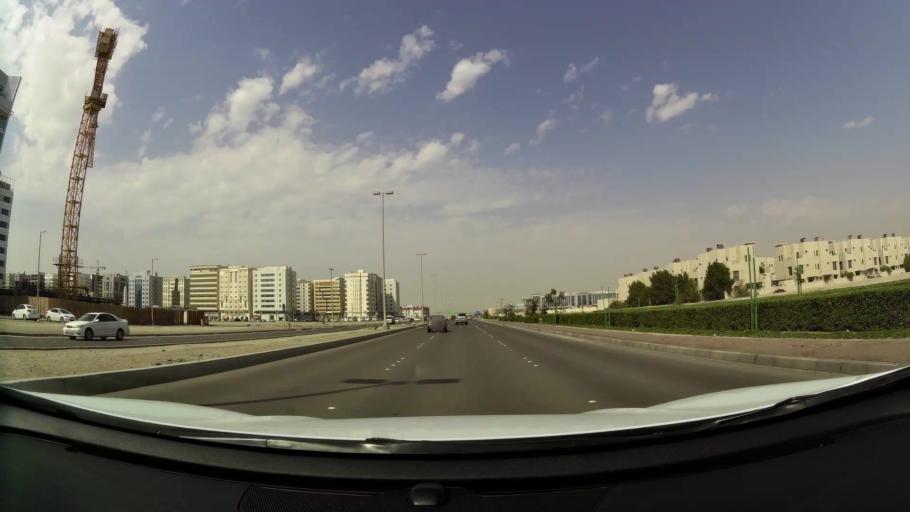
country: AE
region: Abu Dhabi
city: Abu Dhabi
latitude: 24.3414
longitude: 54.5383
